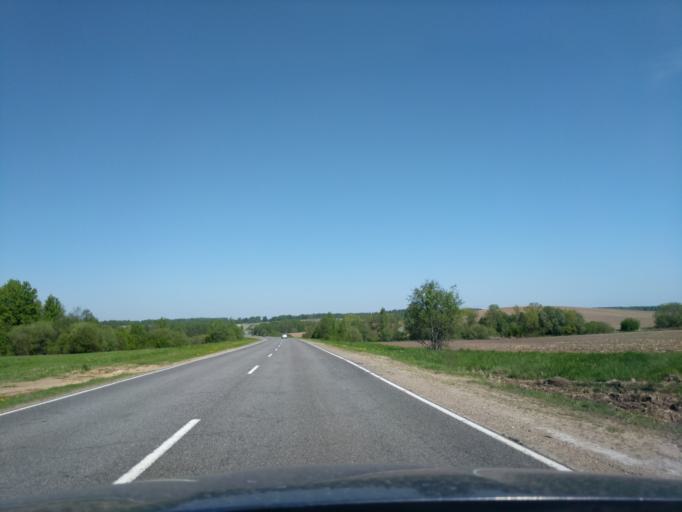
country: BY
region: Minsk
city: Il'ya
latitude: 54.2925
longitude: 27.4840
